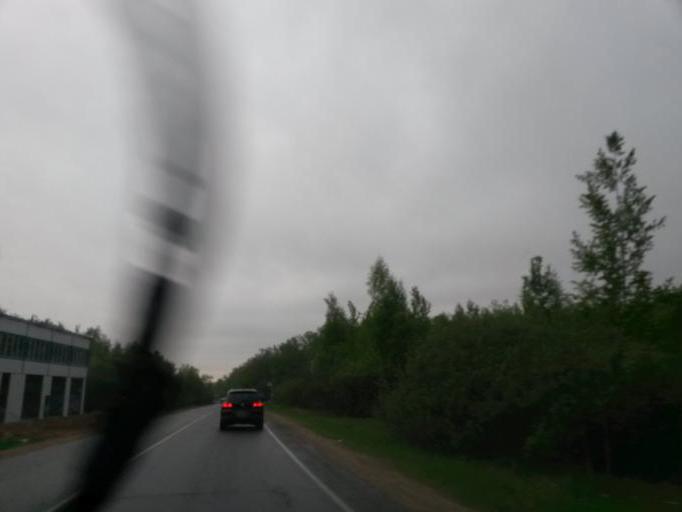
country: RU
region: Moskovskaya
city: Gorki-Leninskiye
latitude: 55.5117
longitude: 37.8059
